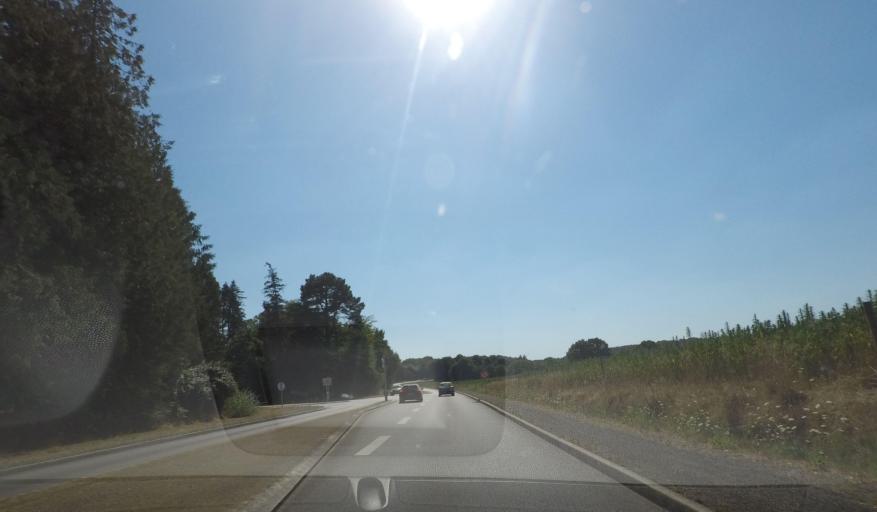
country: FR
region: Brittany
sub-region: Departement du Morbihan
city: Malestroit
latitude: 47.8000
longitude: -2.4061
